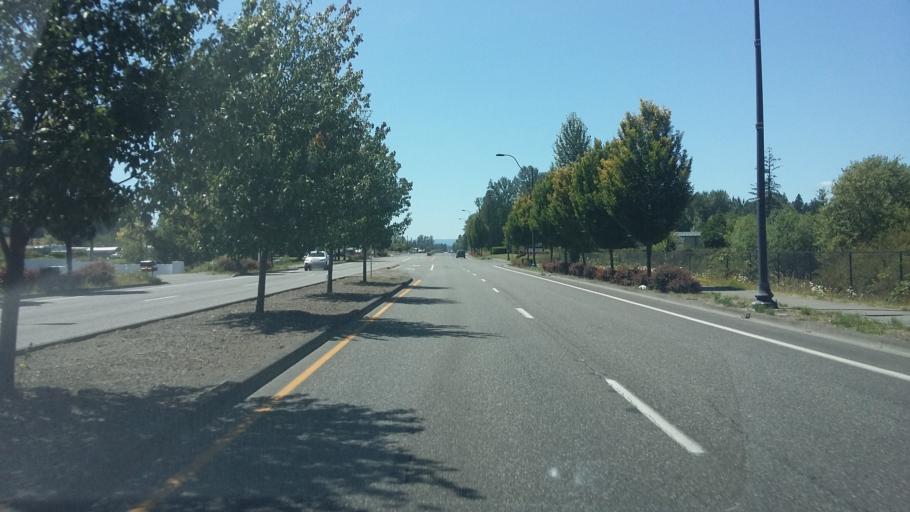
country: US
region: Washington
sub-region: Clark County
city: Meadow Glade
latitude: 45.7806
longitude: -122.5657
